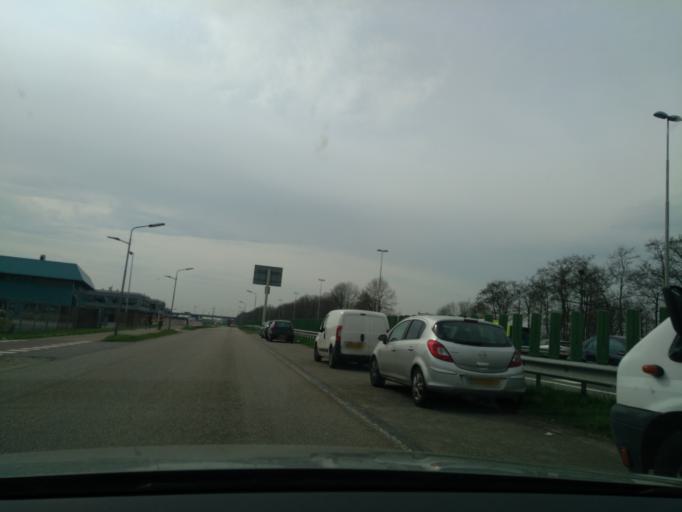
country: NL
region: North Holland
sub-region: Gemeente Haarlem
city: Haarlem
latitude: 52.3860
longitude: 4.7219
